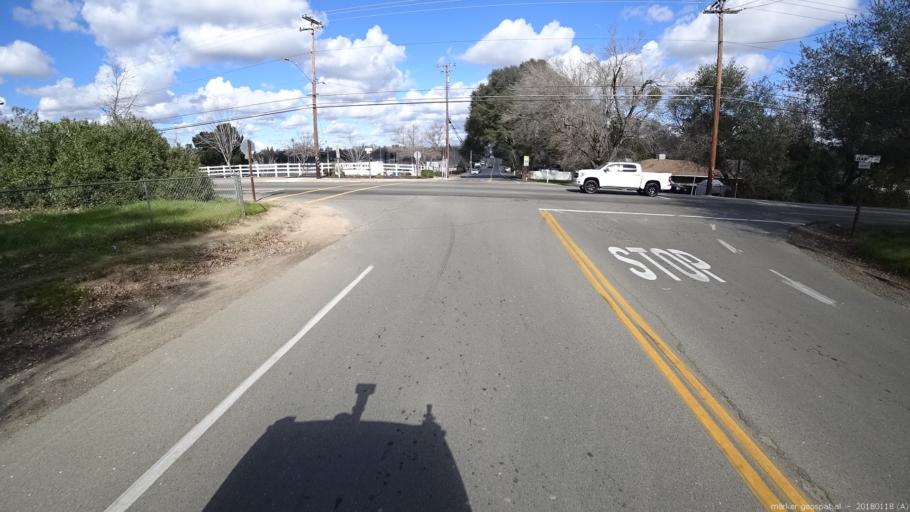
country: US
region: California
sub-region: Sacramento County
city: Orangevale
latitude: 38.6999
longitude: -121.2111
